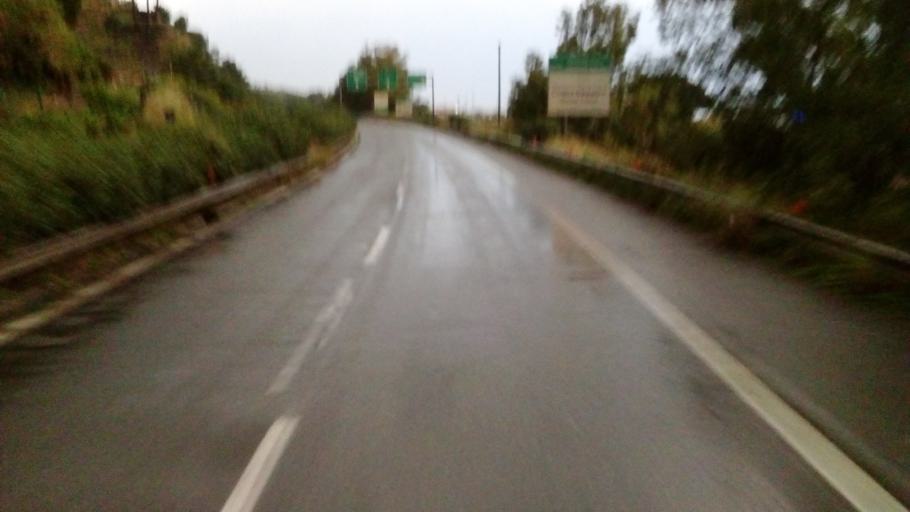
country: IT
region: Sicily
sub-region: Messina
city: Larderia
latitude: 38.1274
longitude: 15.5183
